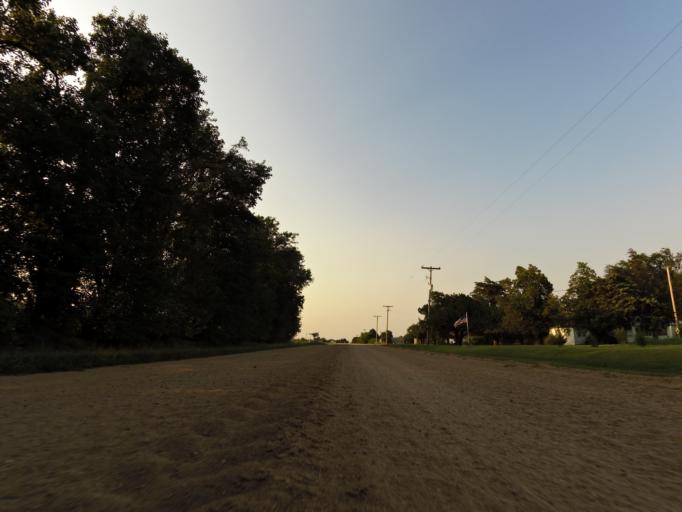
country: US
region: Kansas
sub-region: Reno County
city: South Hutchinson
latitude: 37.9984
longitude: -97.9955
